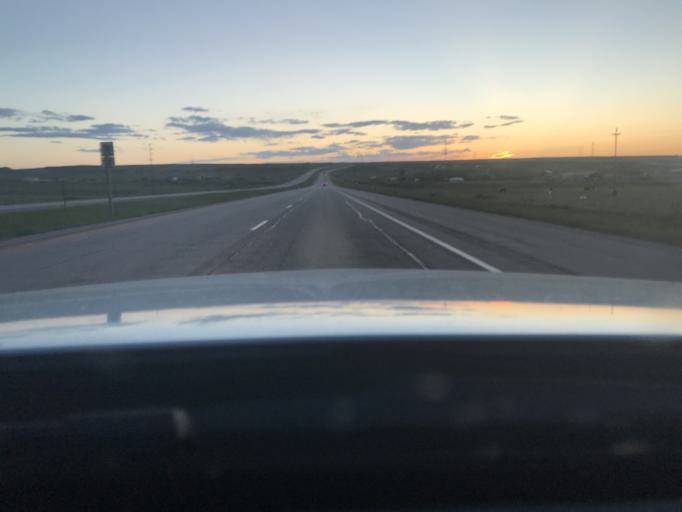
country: US
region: Wyoming
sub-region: Converse County
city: Glenrock
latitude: 42.8257
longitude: -105.8094
